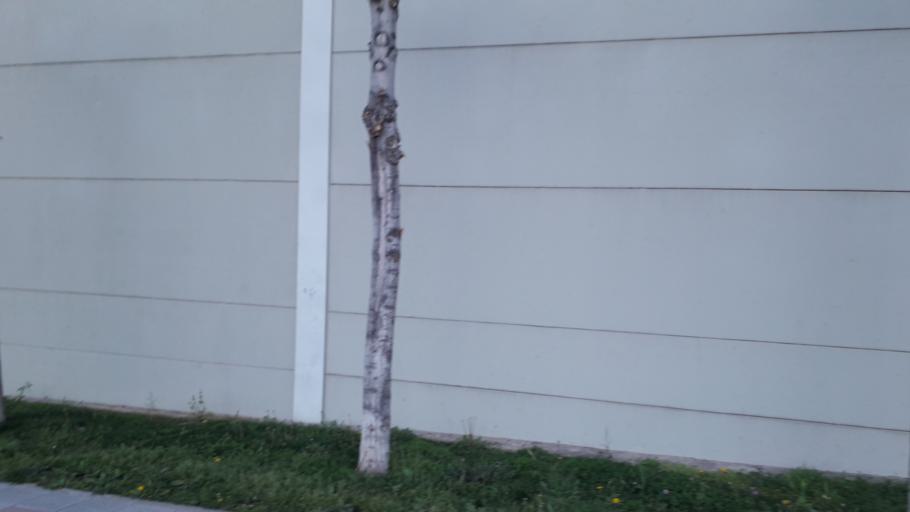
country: ES
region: Madrid
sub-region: Provincia de Madrid
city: El Molar
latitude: 40.7395
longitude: -3.5810
